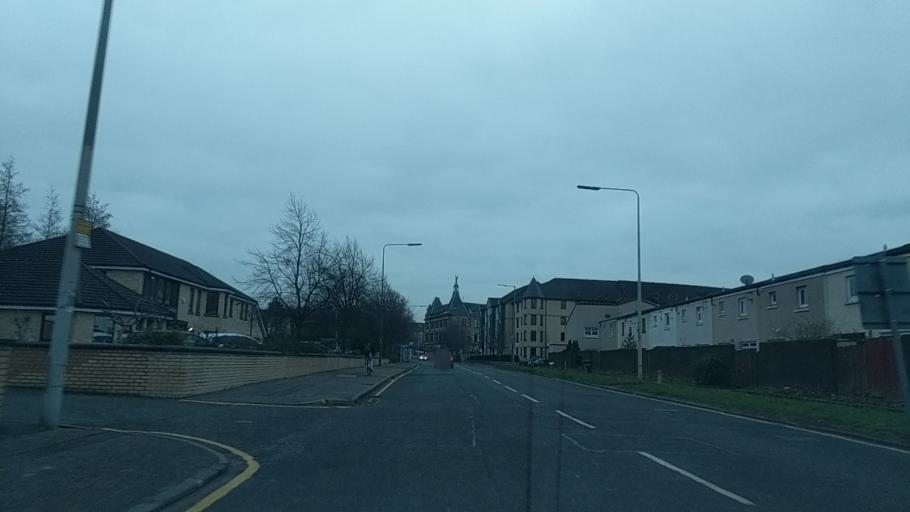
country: GB
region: Scotland
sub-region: Glasgow City
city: Glasgow
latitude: 55.8552
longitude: -4.2824
